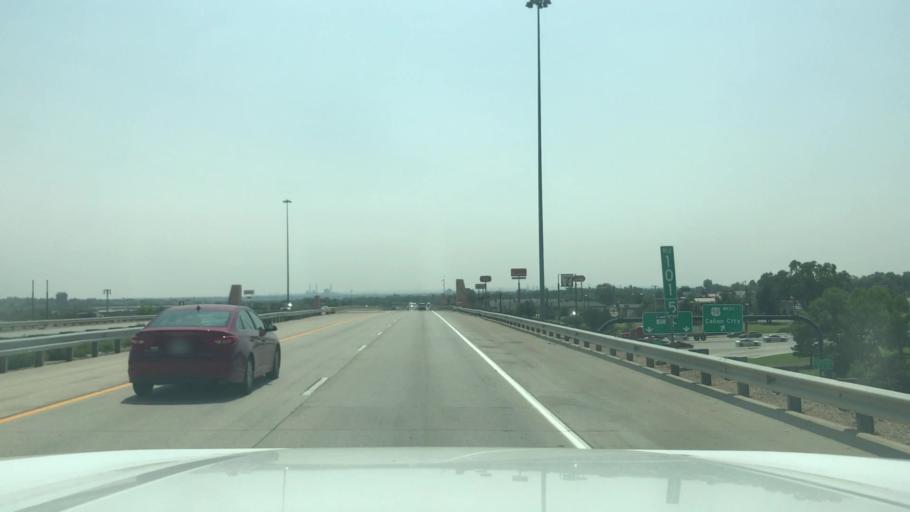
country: US
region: Colorado
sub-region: Pueblo County
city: Pueblo
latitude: 38.3093
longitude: -104.6144
